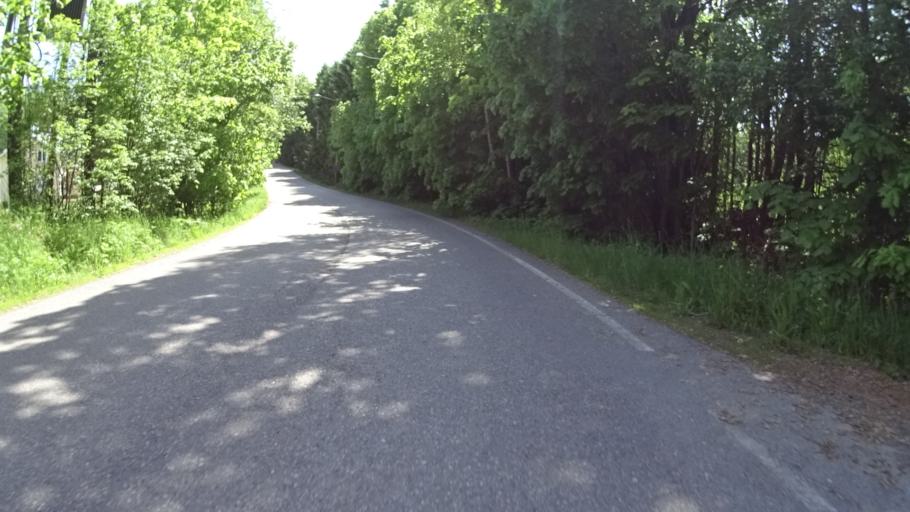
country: FI
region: Uusimaa
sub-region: Helsinki
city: Espoo
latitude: 60.2763
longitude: 24.6697
